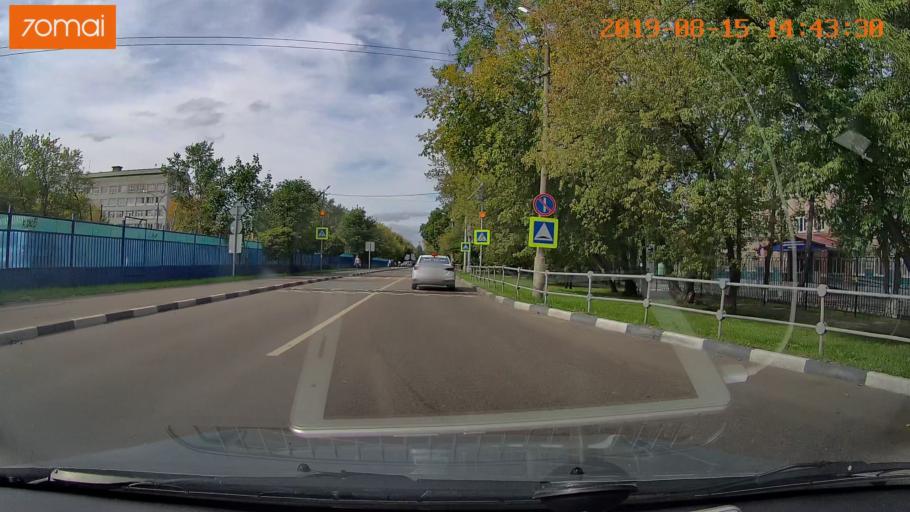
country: RU
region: Moskovskaya
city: Lyubertsy
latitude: 55.6657
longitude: 37.9067
